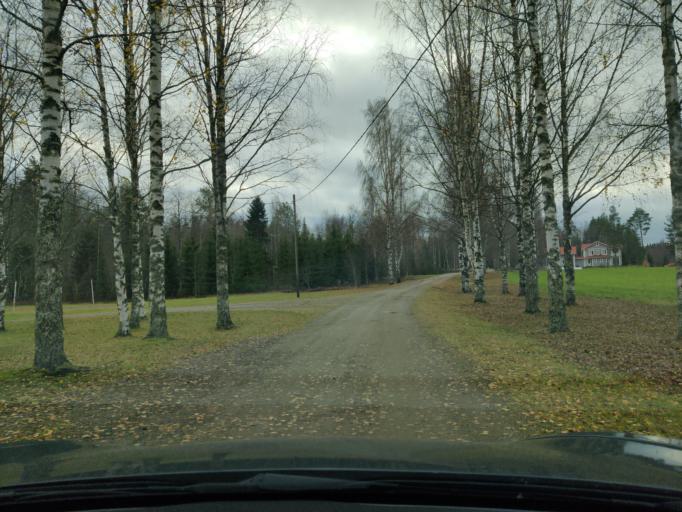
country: FI
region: Northern Savo
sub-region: Ylae-Savo
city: Kiuruvesi
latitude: 63.6417
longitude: 26.6541
